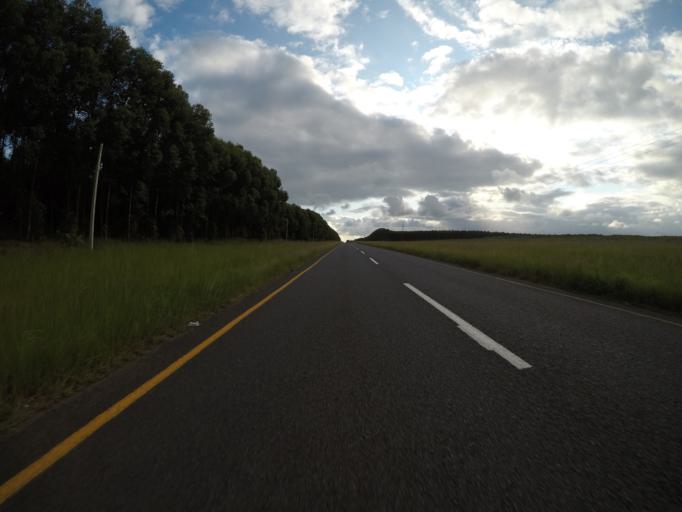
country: ZA
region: KwaZulu-Natal
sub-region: uMkhanyakude District Municipality
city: Mtubatuba
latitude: -28.3895
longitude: 32.2297
